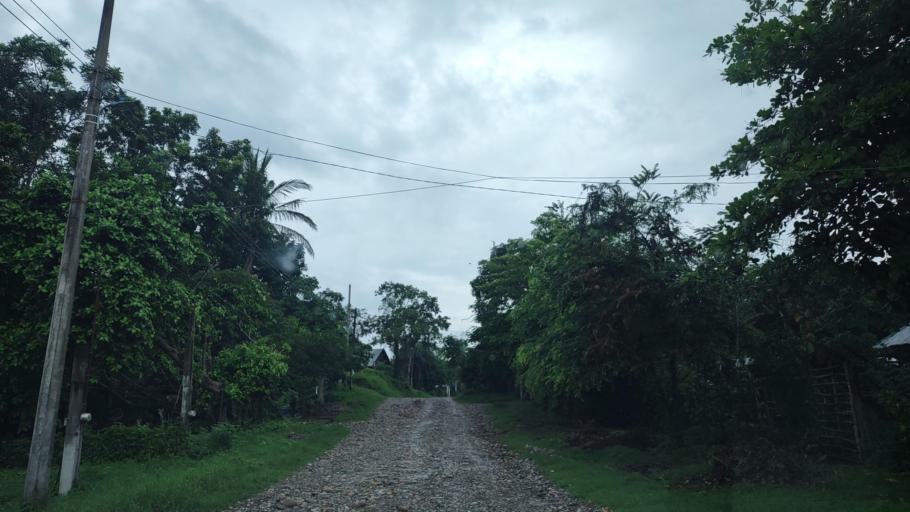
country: MX
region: San Luis Potosi
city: Tanquian de Escobedo
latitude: 21.5424
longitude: -98.5515
